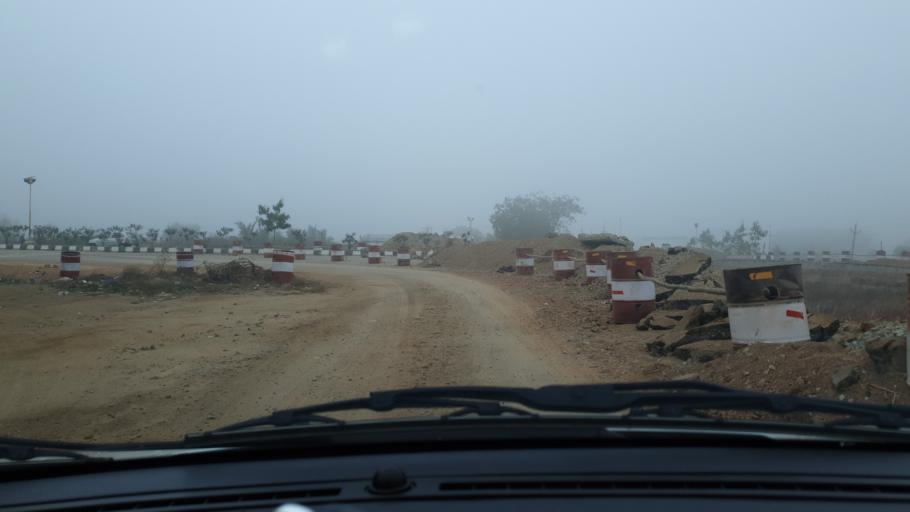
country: IN
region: Telangana
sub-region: Mahbubnagar
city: Nagar Karnul
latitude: 16.6612
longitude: 78.5773
